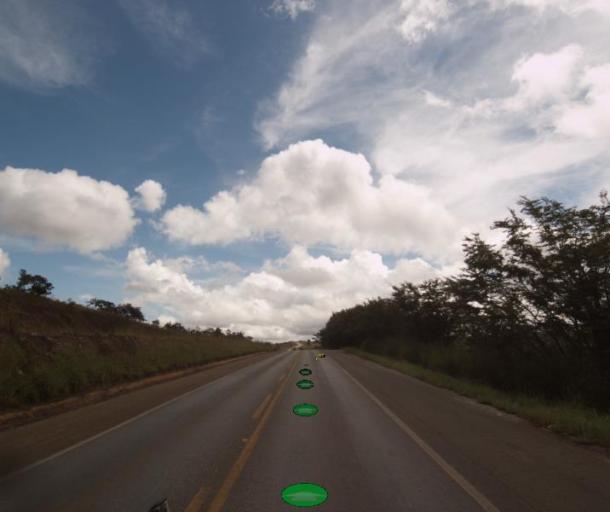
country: BR
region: Federal District
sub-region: Brasilia
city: Brasilia
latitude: -15.7437
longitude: -48.3628
